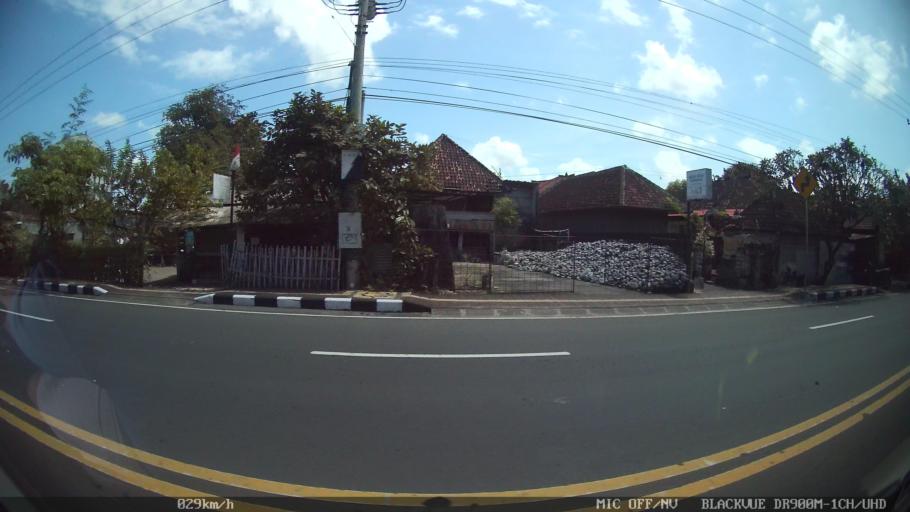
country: ID
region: Bali
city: Denpasar
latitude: -8.6646
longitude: 115.1899
